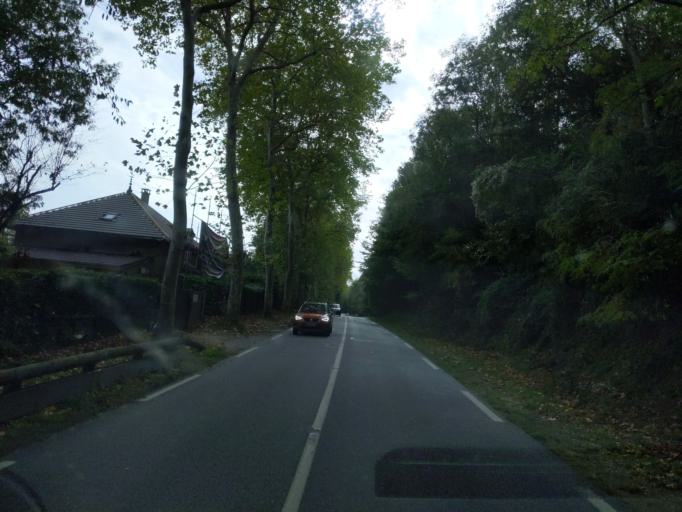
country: FR
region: Ile-de-France
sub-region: Departement des Yvelines
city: Chevreuse
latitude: 48.6948
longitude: 2.0185
